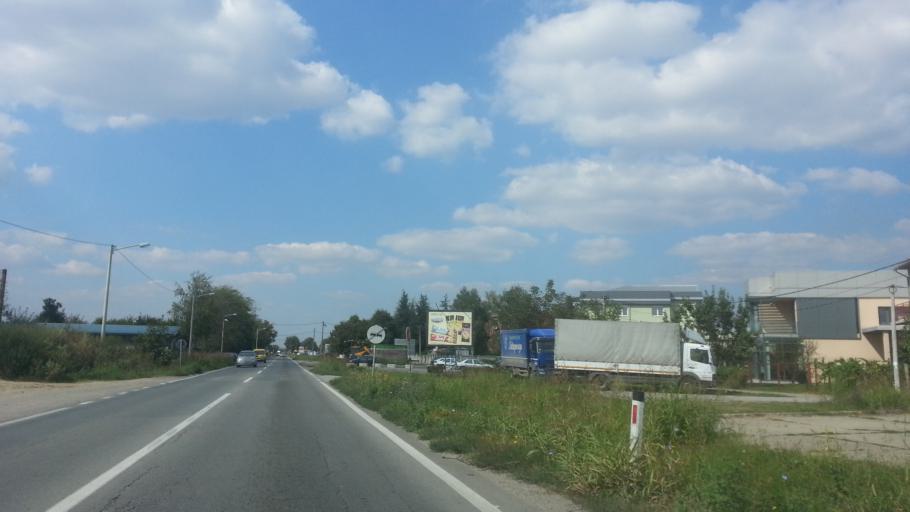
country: RS
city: Novi Banovci
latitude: 44.8902
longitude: 20.3069
